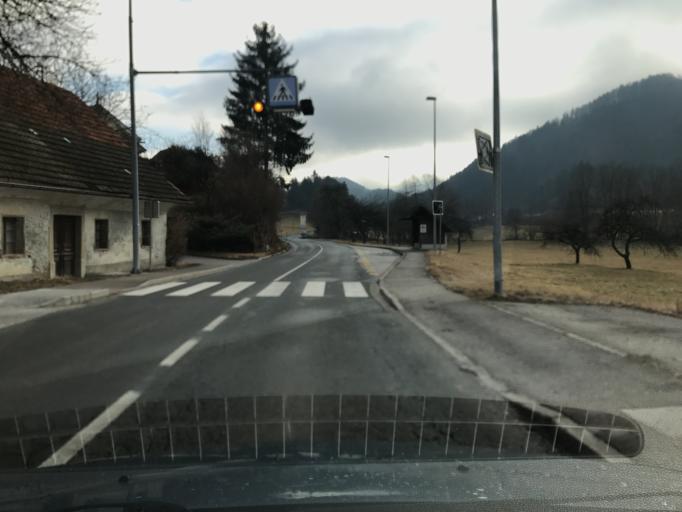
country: SI
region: Lukovica
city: Lukovica pri Domzalah
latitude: 46.2162
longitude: 14.7230
